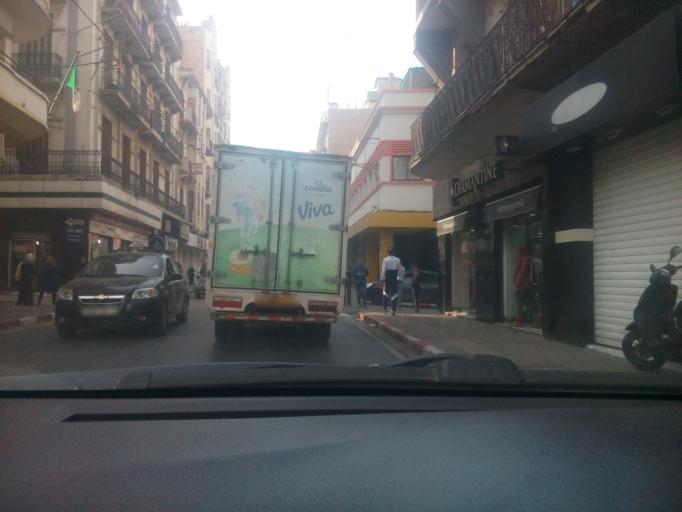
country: DZ
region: Oran
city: Oran
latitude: 35.7039
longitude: -0.6346
